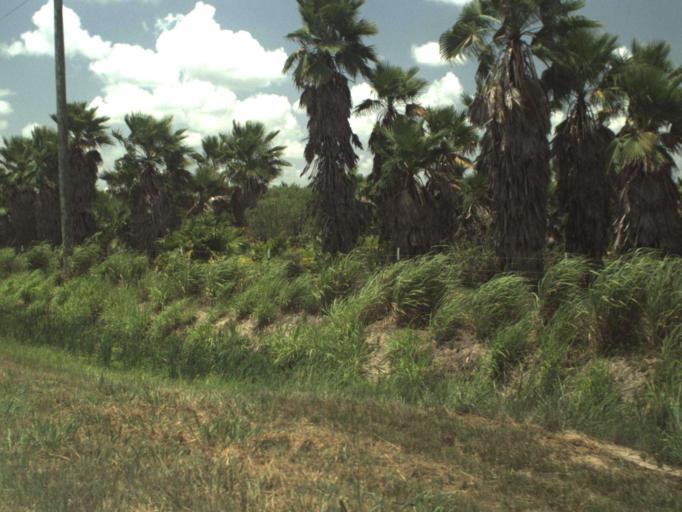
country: US
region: Florida
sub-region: Saint Lucie County
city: Fort Pierce South
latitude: 27.3745
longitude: -80.4776
